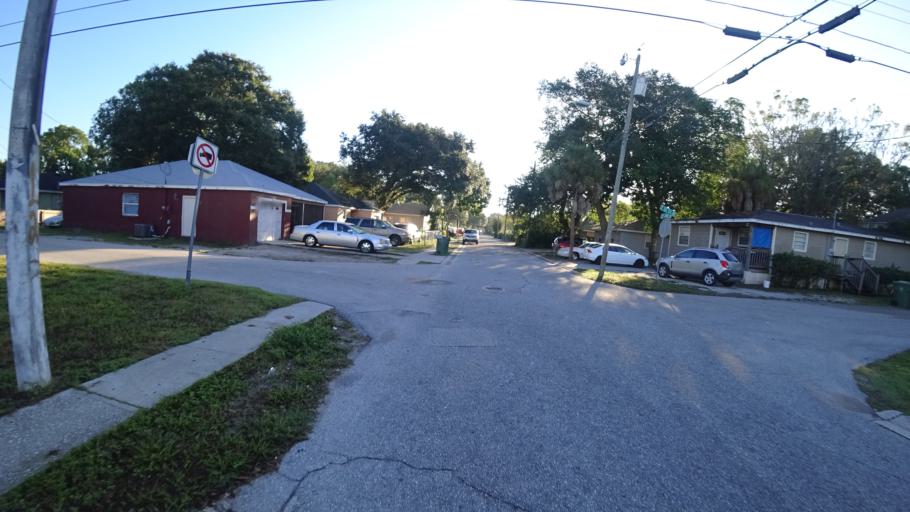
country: US
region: Florida
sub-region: Manatee County
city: Bradenton
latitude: 27.4891
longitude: -82.5697
